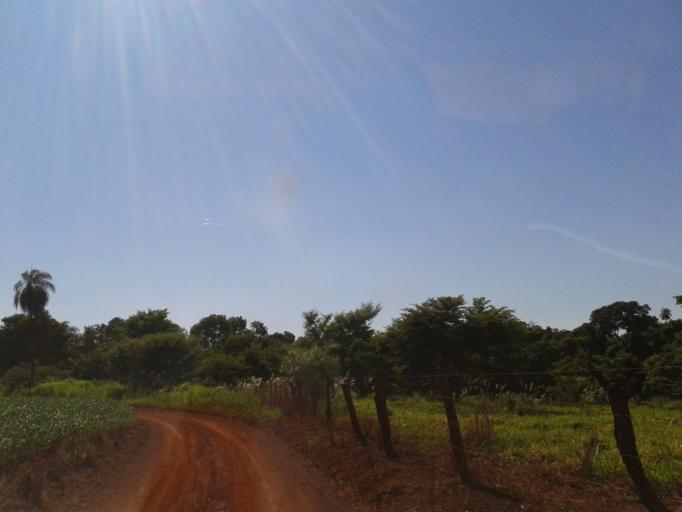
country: BR
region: Minas Gerais
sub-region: Centralina
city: Centralina
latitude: -18.6186
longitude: -49.2908
